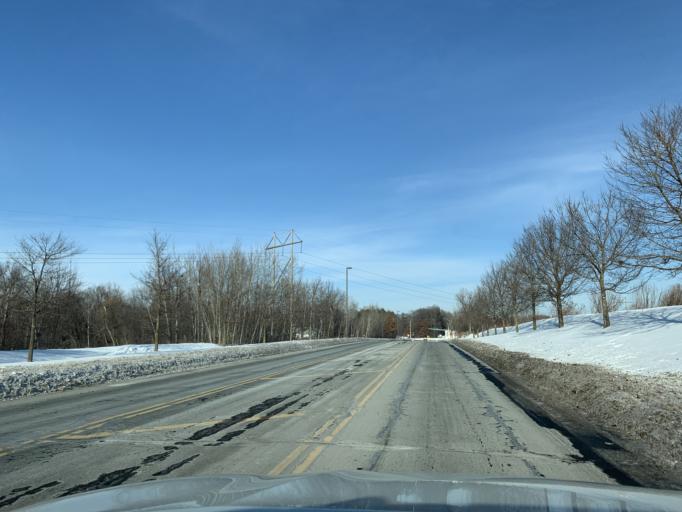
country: US
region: Minnesota
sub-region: Anoka County
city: Columbus
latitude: 45.2478
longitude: -93.0349
